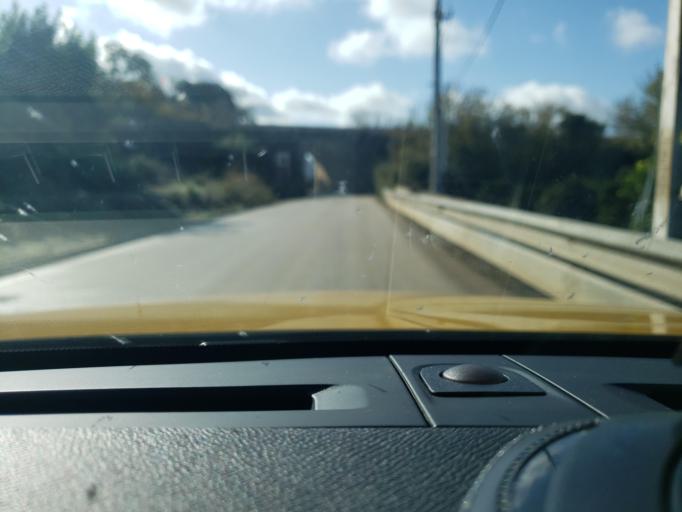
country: PT
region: Faro
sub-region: Portimao
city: Alvor
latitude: 37.1710
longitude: -8.5792
